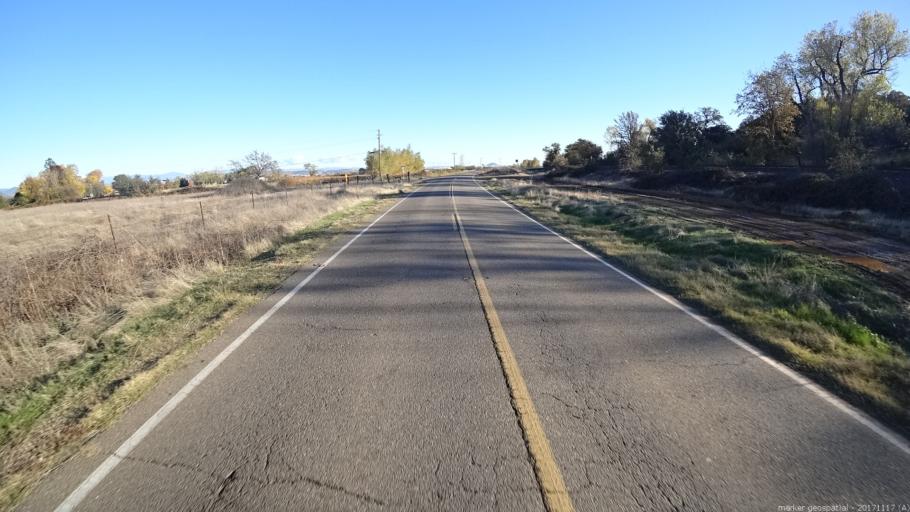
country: US
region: California
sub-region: Shasta County
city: Cottonwood
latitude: 40.4161
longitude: -122.2504
